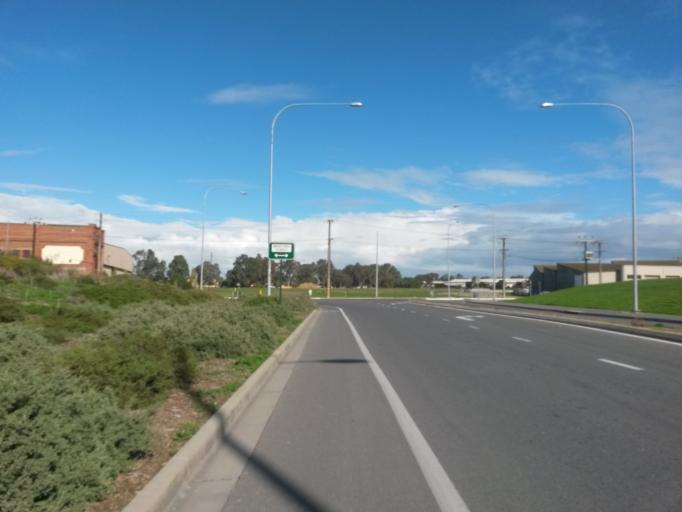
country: AU
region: South Australia
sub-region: Port Adelaide Enfield
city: Alberton
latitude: -34.8453
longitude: 138.5149
